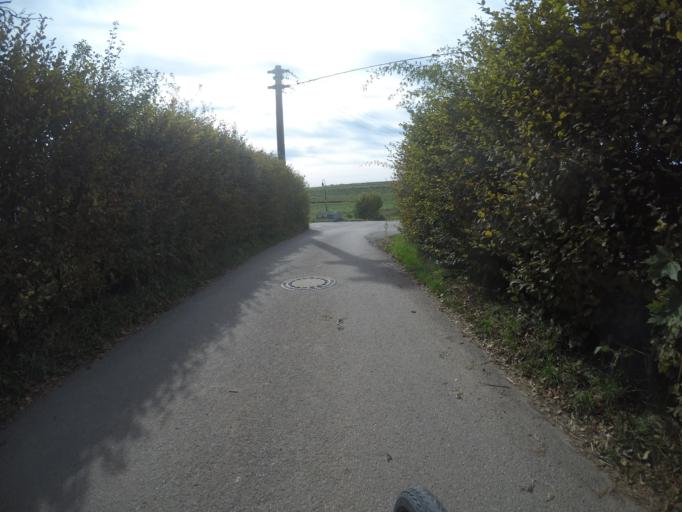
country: DE
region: Baden-Wuerttemberg
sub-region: Regierungsbezirk Stuttgart
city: Deckenpfronn
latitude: 48.6449
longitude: 8.8429
